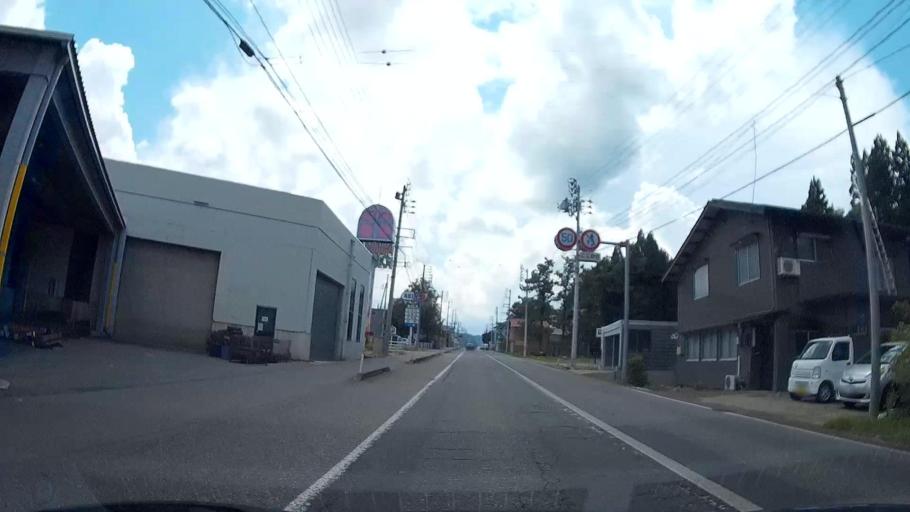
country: JP
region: Niigata
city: Tokamachi
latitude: 37.0265
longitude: 138.6638
